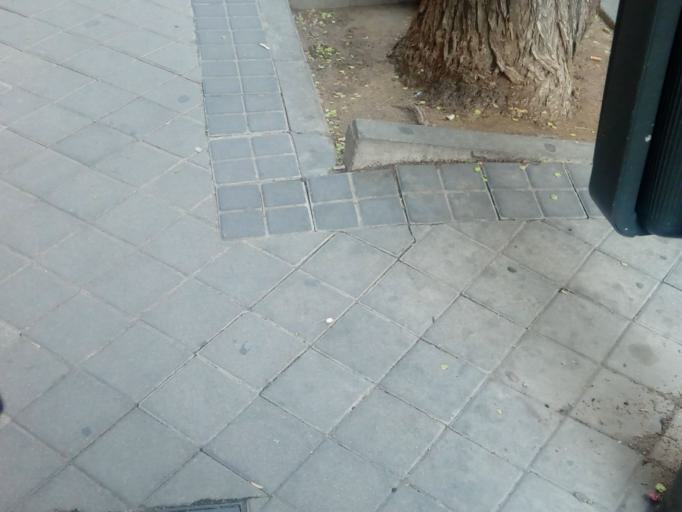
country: ES
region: Madrid
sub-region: Provincia de Madrid
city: Retiro
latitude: 40.4032
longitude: -3.6754
